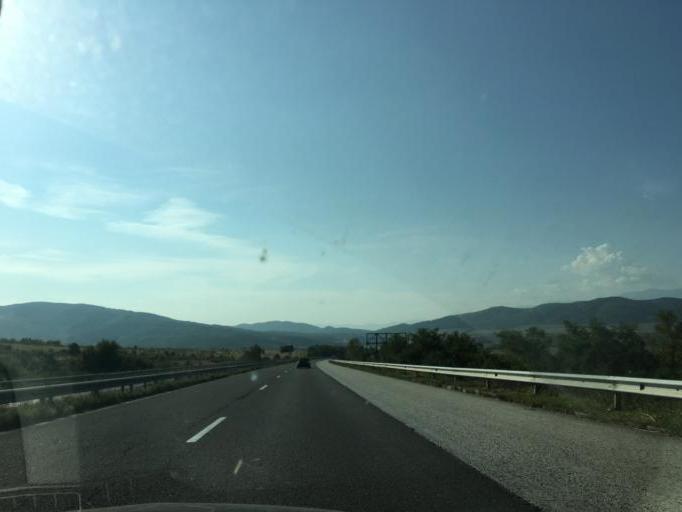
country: BG
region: Sofiya
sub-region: Obshtina Ikhtiman
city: Ikhtiman
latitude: 42.4224
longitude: 23.8568
